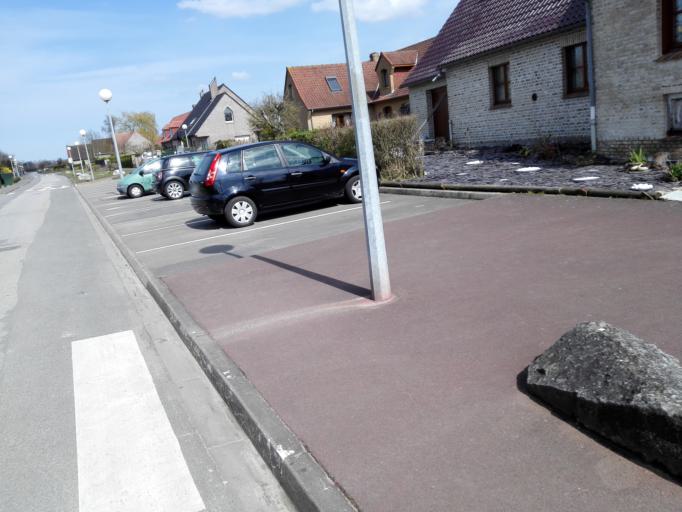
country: FR
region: Nord-Pas-de-Calais
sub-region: Departement du Nord
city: Brouckerque
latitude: 50.9548
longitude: 2.2928
